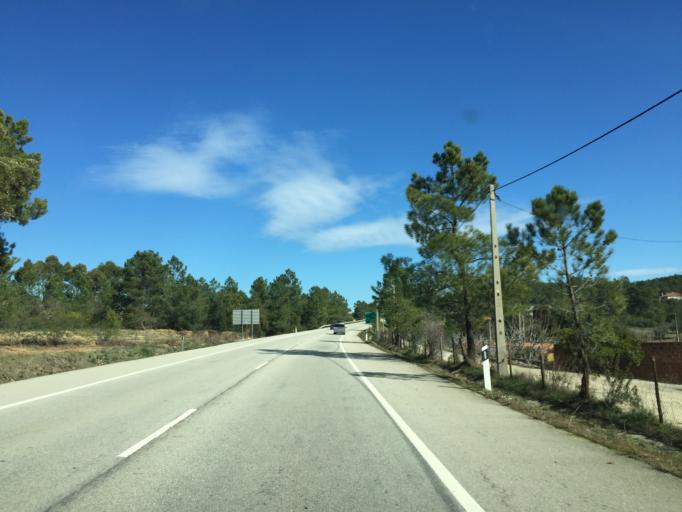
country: PT
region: Castelo Branco
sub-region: Castelo Branco
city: Castelo Branco
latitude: 39.7658
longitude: -7.5955
